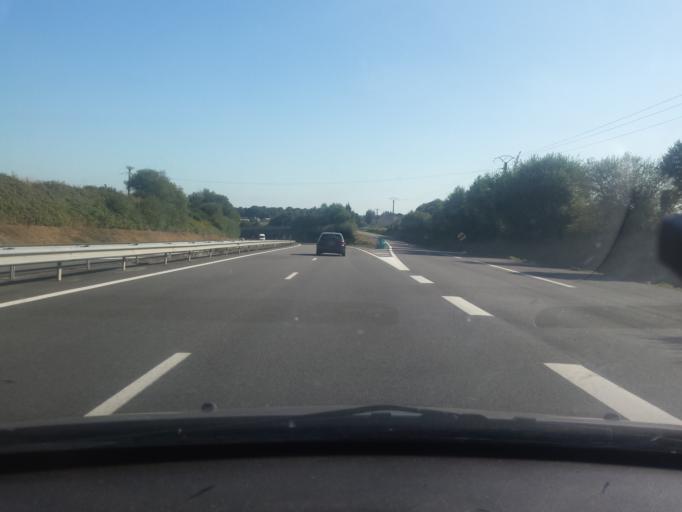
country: FR
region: Brittany
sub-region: Departement du Morbihan
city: Saint-Thuriau
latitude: 48.0083
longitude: -2.9048
